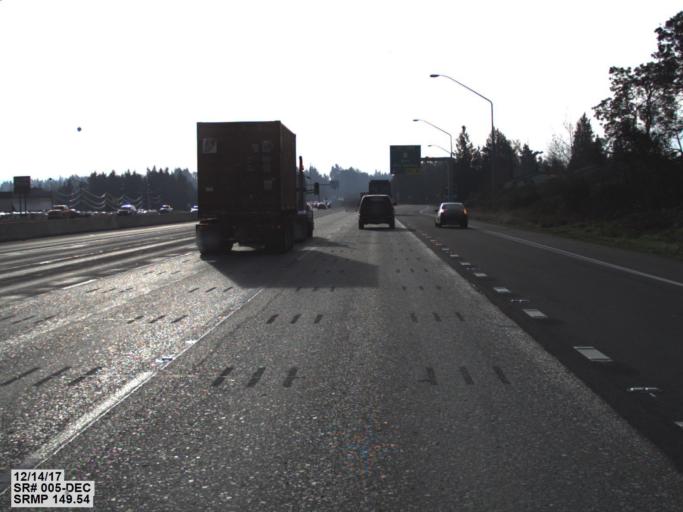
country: US
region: Washington
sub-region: King County
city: Des Moines
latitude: 47.3967
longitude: -122.2919
